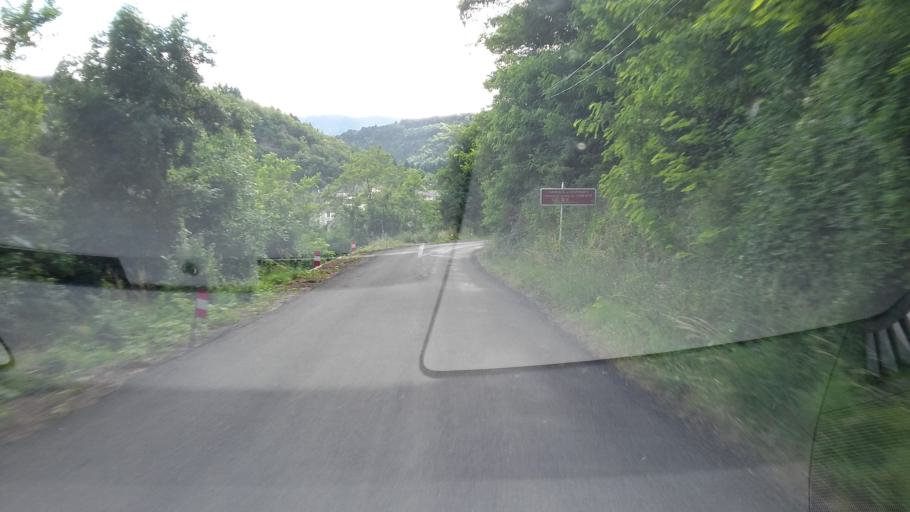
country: FR
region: Languedoc-Roussillon
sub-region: Departement de la Lozere
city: Meyrueis
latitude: 44.0249
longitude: 3.3636
